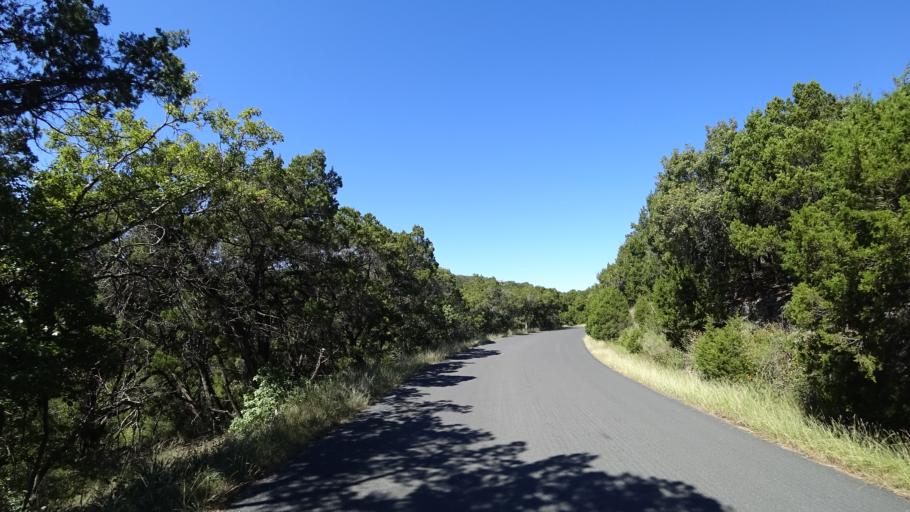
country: US
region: Texas
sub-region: Travis County
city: West Lake Hills
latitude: 30.3084
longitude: -97.8045
